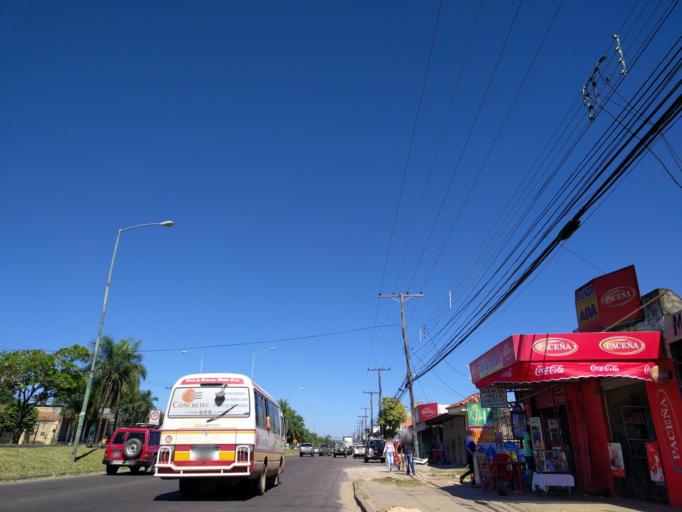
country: BO
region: Santa Cruz
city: Santa Cruz de la Sierra
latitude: -17.8251
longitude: -63.2234
